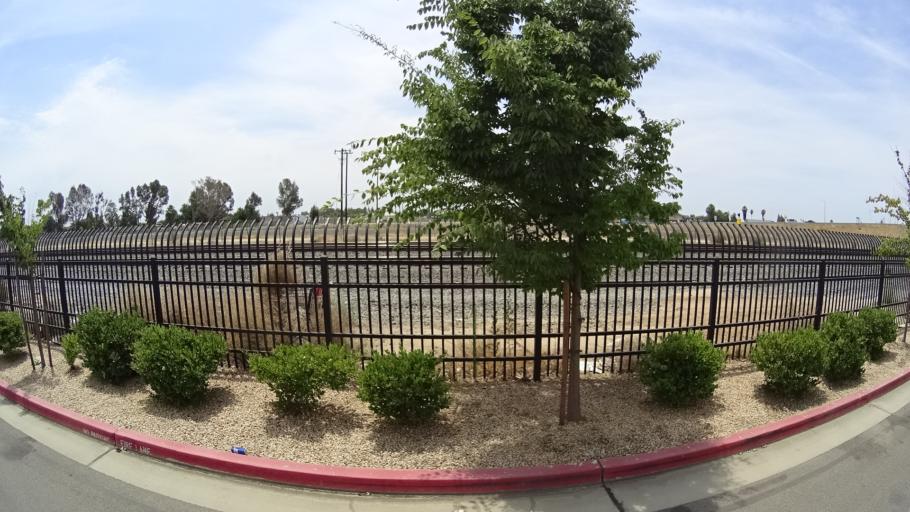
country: US
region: California
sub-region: Fresno County
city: West Park
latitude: 36.7704
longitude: -119.8352
